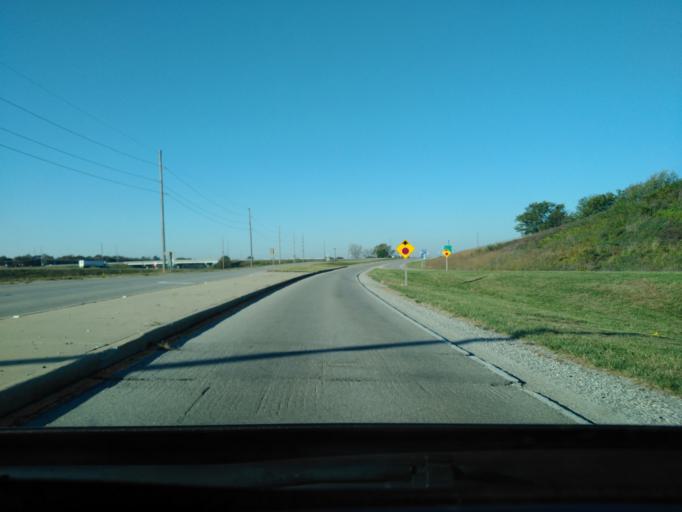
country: US
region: Illinois
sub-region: Bond County
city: Greenville
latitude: 38.8562
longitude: -89.4471
